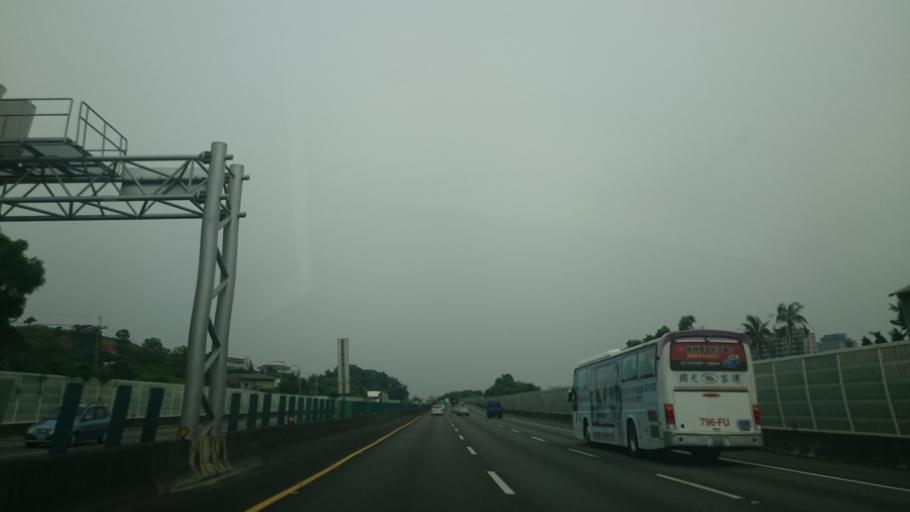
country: TW
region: Taiwan
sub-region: Changhua
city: Chang-hua
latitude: 24.1156
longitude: 120.5932
